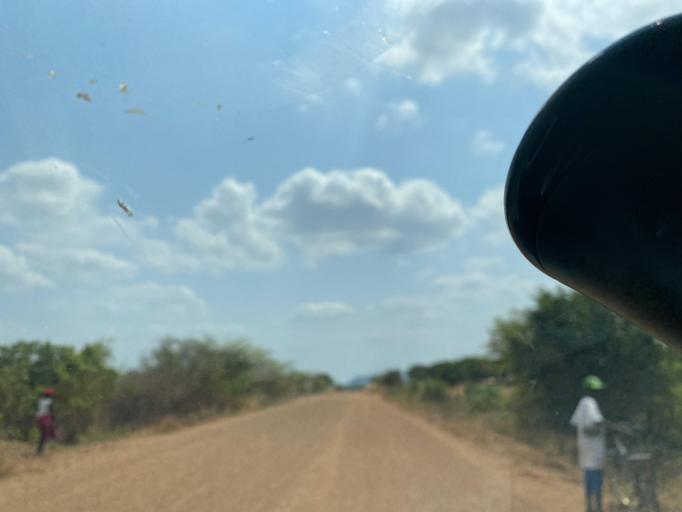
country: ZM
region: Lusaka
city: Chongwe
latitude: -15.5913
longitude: 28.7974
